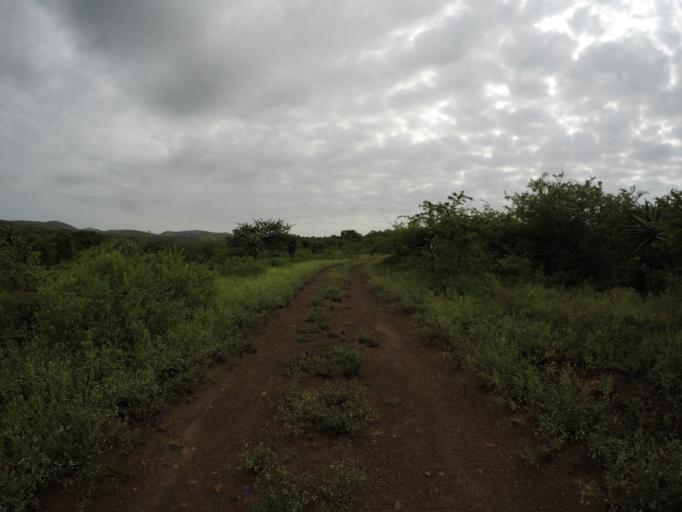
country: ZA
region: KwaZulu-Natal
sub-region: uThungulu District Municipality
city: Empangeni
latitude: -28.6433
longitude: 31.9012
